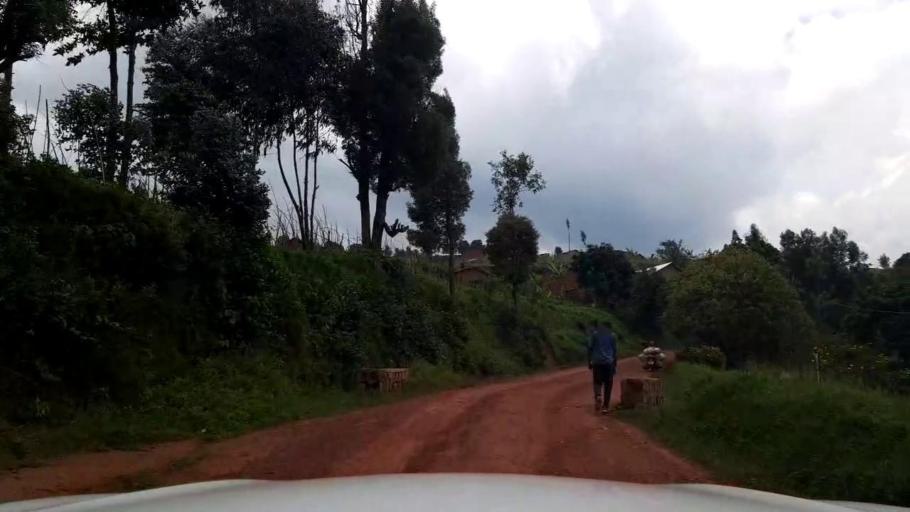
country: RW
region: Northern Province
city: Byumba
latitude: -1.4885
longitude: 29.9102
